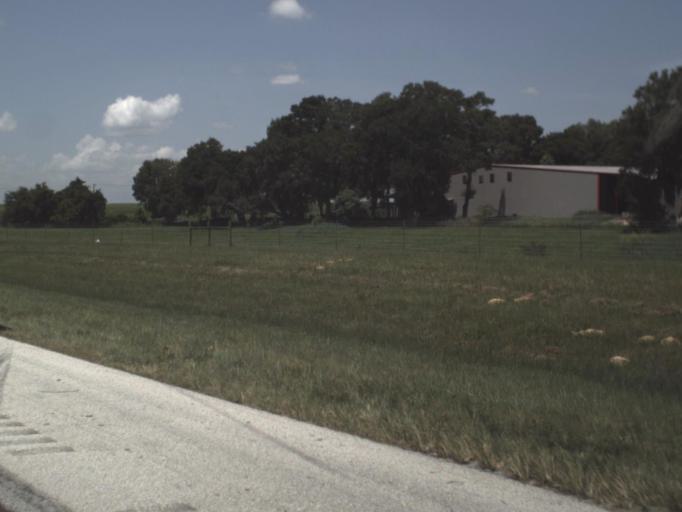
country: US
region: Florida
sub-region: Hillsborough County
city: Seffner
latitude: 28.0092
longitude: -82.2873
